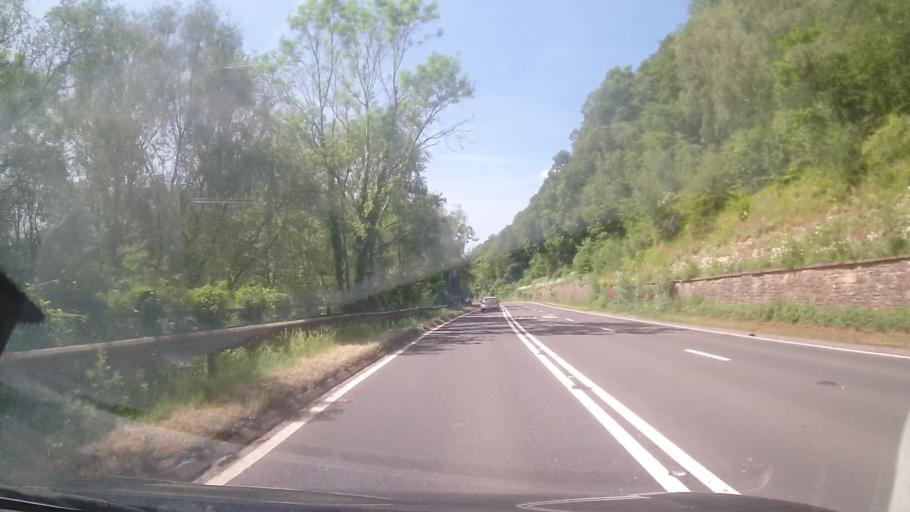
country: GB
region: England
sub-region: Herefordshire
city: Hope under Dinmore
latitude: 52.1539
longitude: -2.7188
